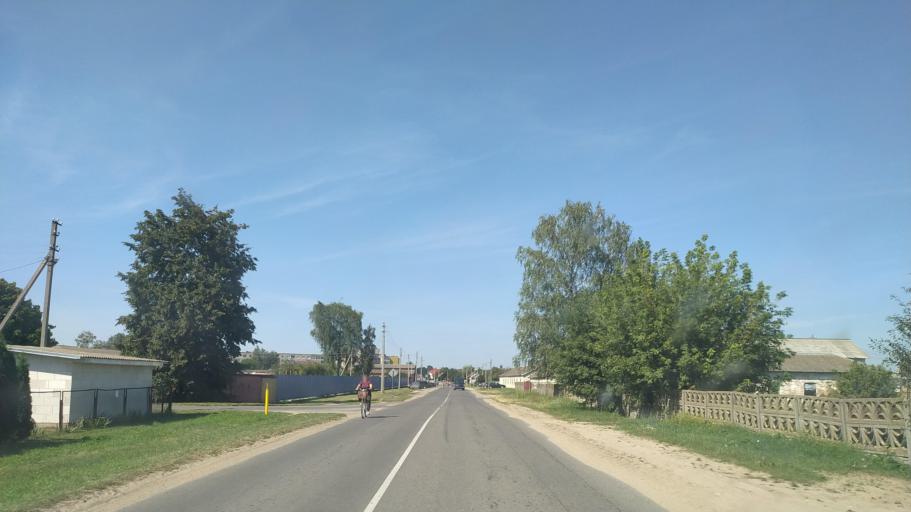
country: BY
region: Brest
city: Byaroza
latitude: 52.5246
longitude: 24.9894
